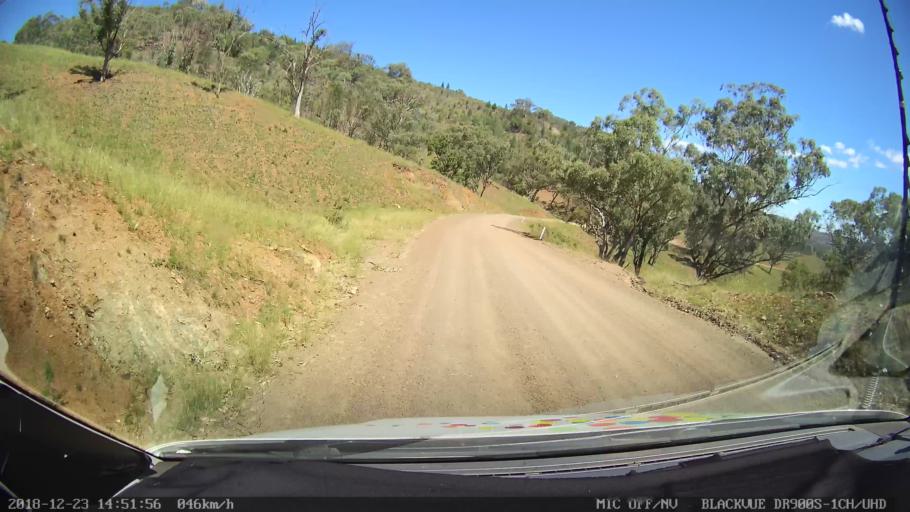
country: AU
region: New South Wales
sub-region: Tamworth Municipality
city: Manilla
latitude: -30.6811
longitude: 150.8546
